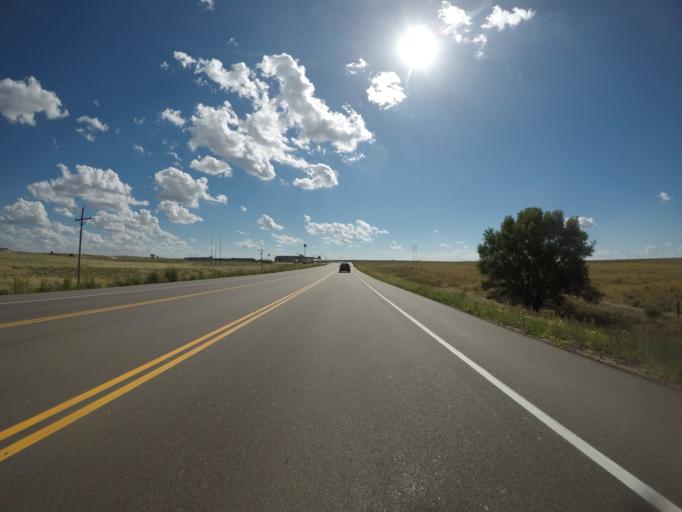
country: US
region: Colorado
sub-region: Logan County
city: Sterling
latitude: 40.6237
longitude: -103.1644
